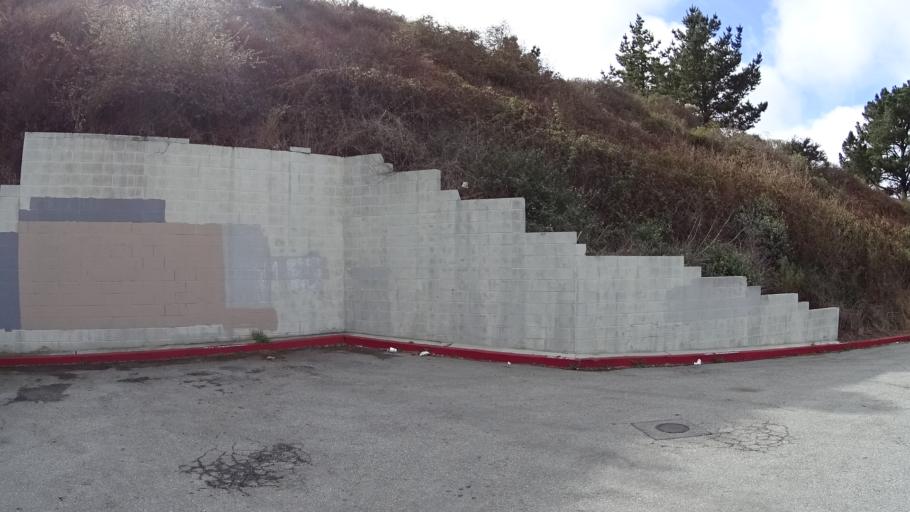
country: US
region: California
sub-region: San Mateo County
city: Daly City
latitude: 37.7051
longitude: -122.4454
